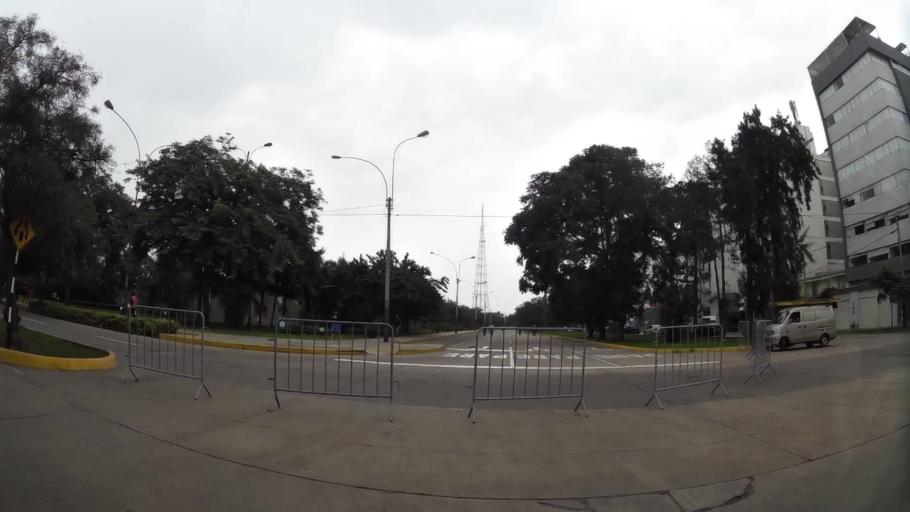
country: PE
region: Lima
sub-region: Lima
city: San Luis
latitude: -12.0975
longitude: -76.9808
